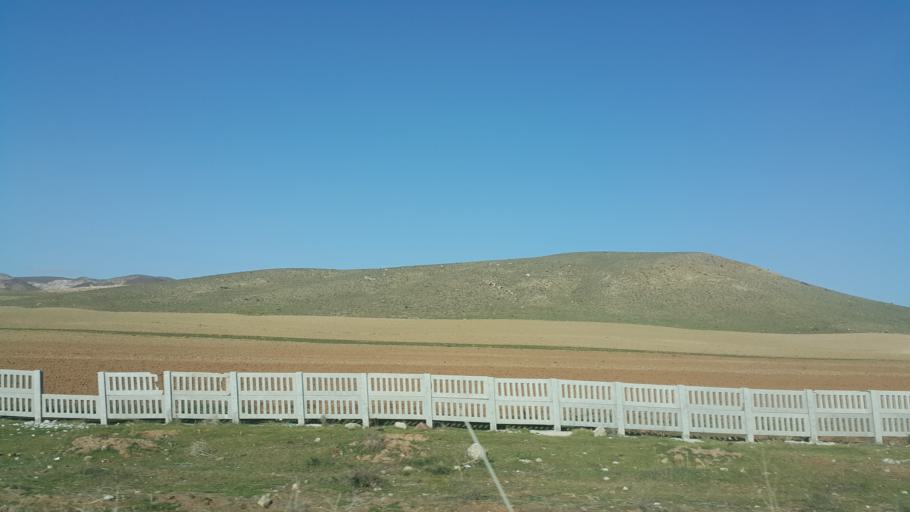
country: TR
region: Aksaray
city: Acipinar
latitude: 38.7093
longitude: 33.6792
